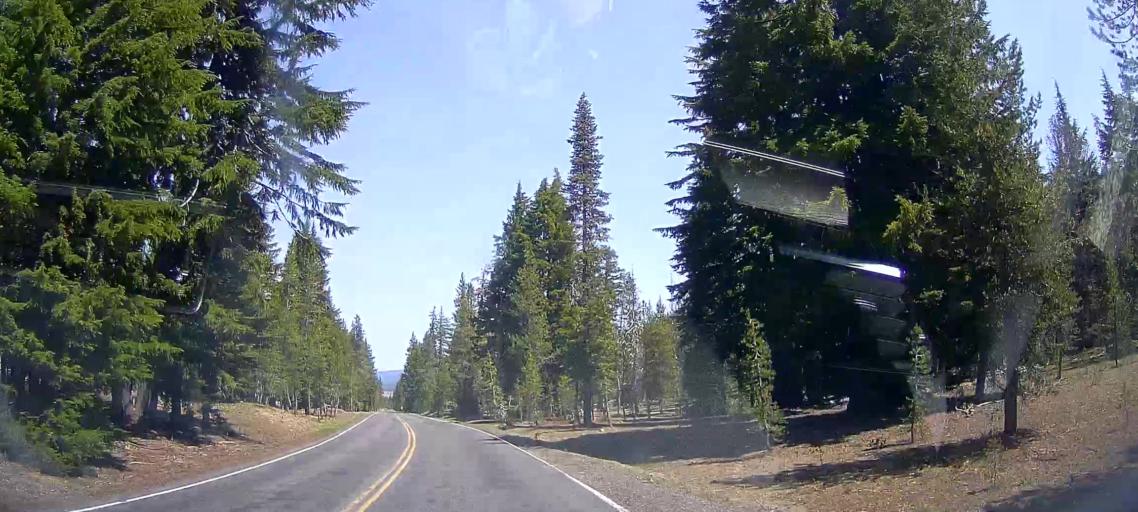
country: US
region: Oregon
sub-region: Jackson County
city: Shady Cove
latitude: 42.9951
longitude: -122.1359
